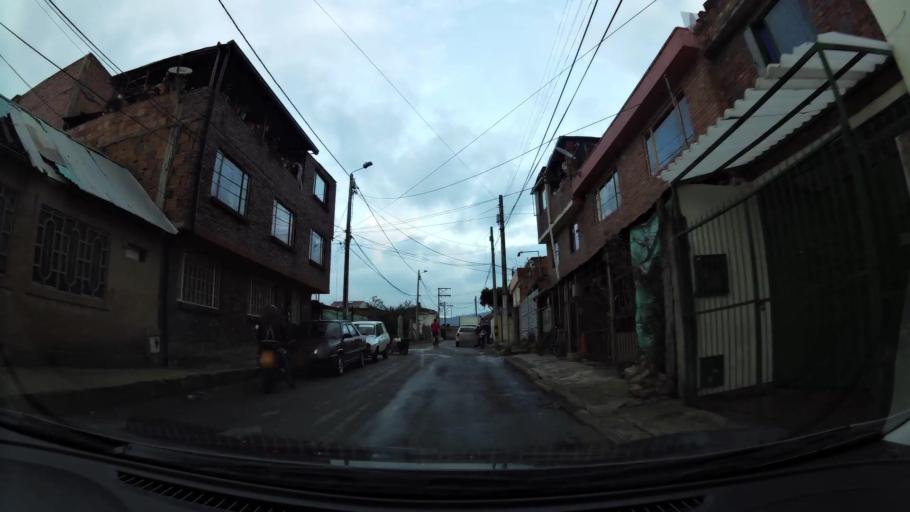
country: CO
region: Cundinamarca
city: Chia
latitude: 4.8638
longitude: -74.0634
